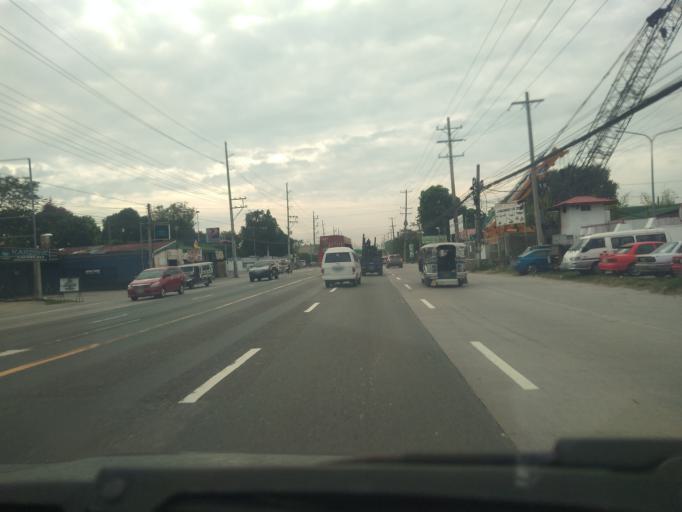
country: PH
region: Central Luzon
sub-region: Province of Pampanga
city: Bulaon
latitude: 15.0609
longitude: 120.6553
